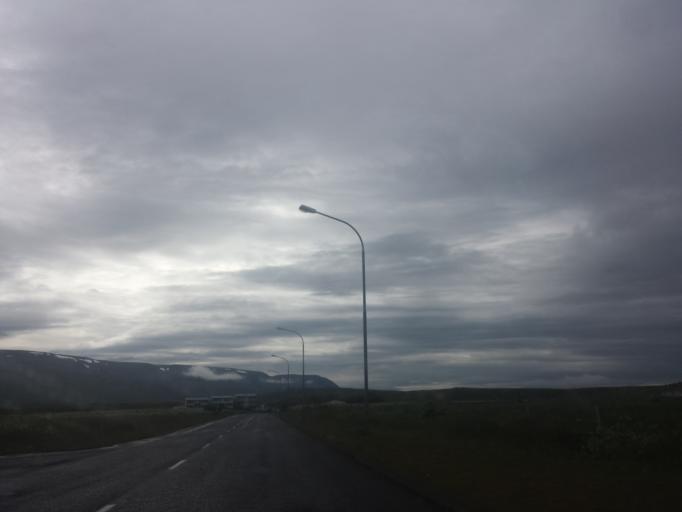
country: IS
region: Northwest
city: Saudarkrokur
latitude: 65.6588
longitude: -20.2973
